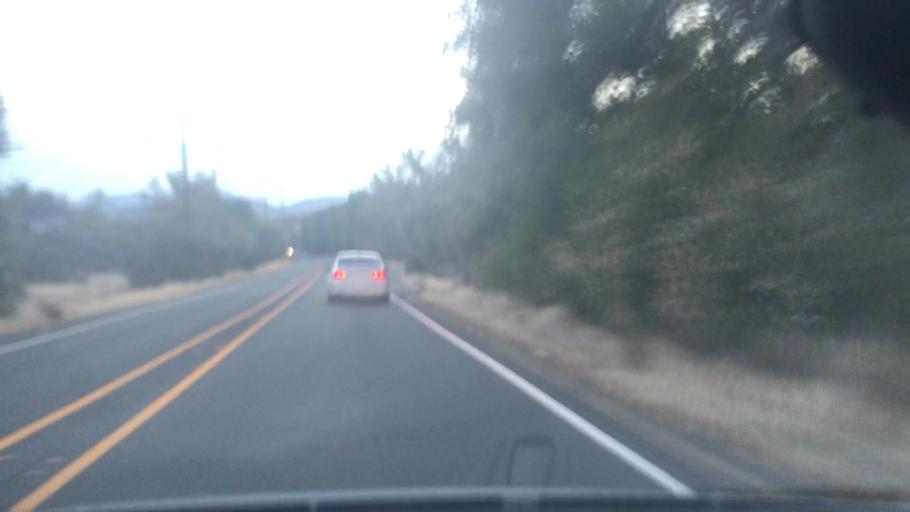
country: US
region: California
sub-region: Orange County
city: Coto De Caza
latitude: 33.5454
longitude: -117.5492
